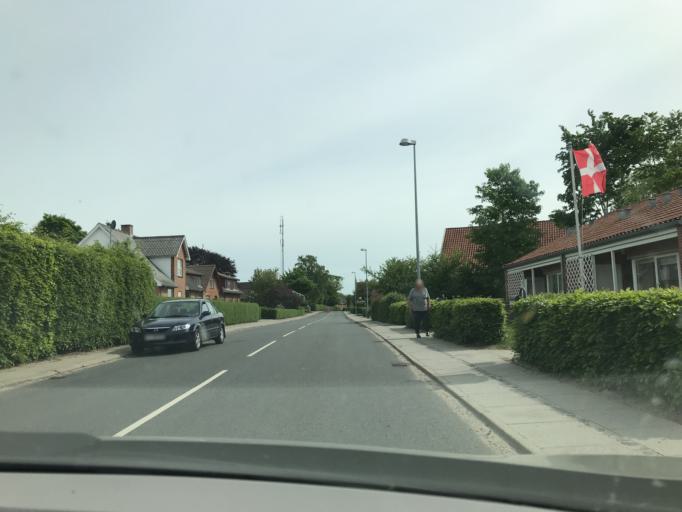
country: DK
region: Central Jutland
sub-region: Norddjurs Kommune
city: Allingabro
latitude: 56.5050
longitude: 10.3350
